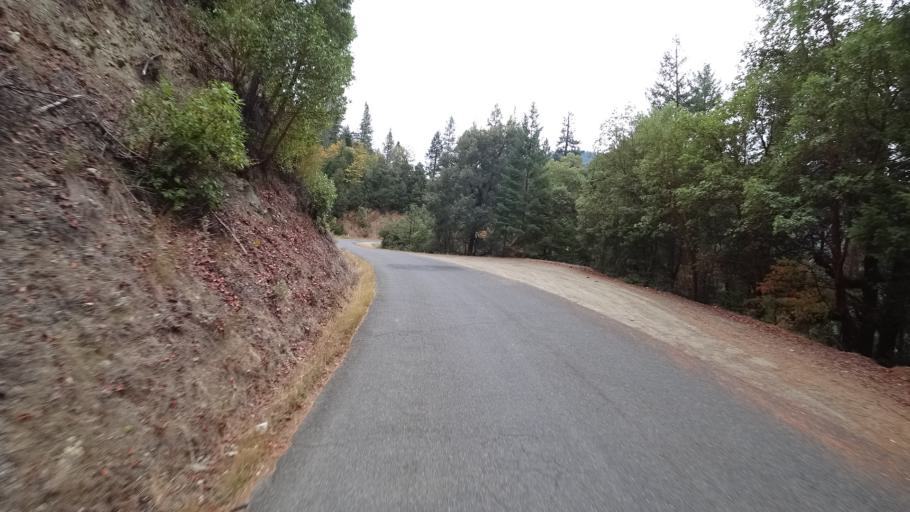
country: US
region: California
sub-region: Siskiyou County
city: Happy Camp
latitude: 41.7788
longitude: -123.3803
